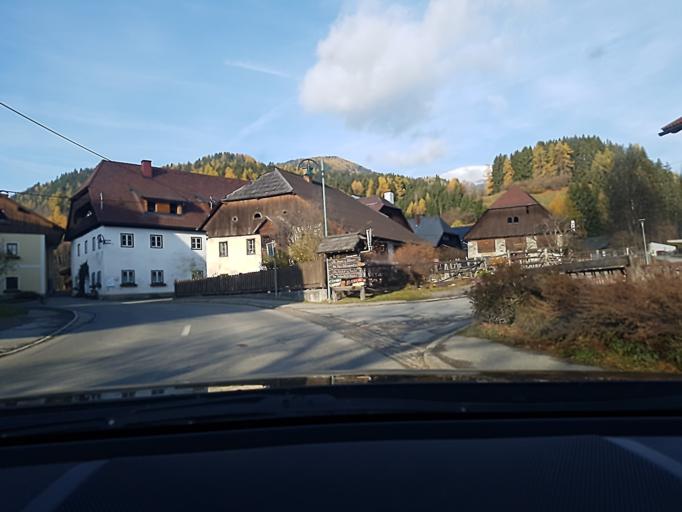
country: AT
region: Styria
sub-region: Politischer Bezirk Murau
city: Schoder
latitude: 47.1907
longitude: 14.1312
